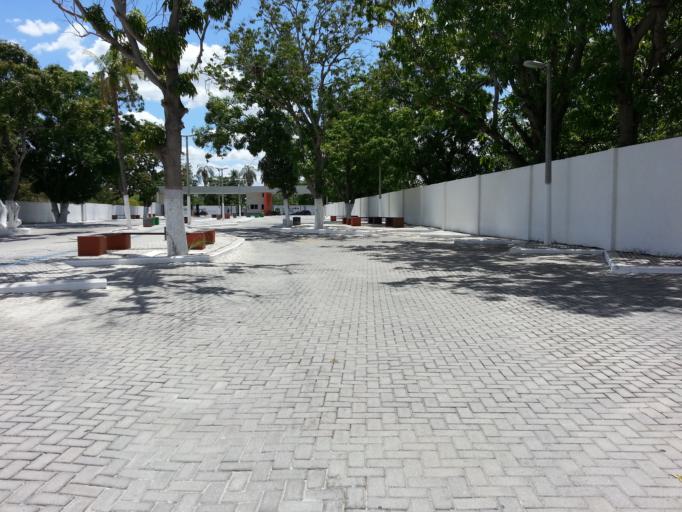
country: BR
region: Ceara
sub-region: Quixada
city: Quixada
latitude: -4.9749
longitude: -39.0150
